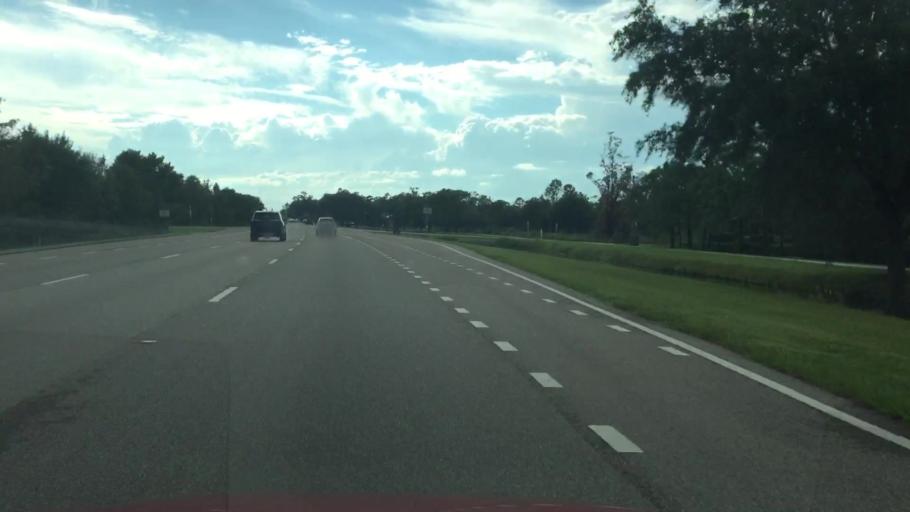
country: US
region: Florida
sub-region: Lee County
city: Villas
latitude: 26.5476
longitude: -81.8111
